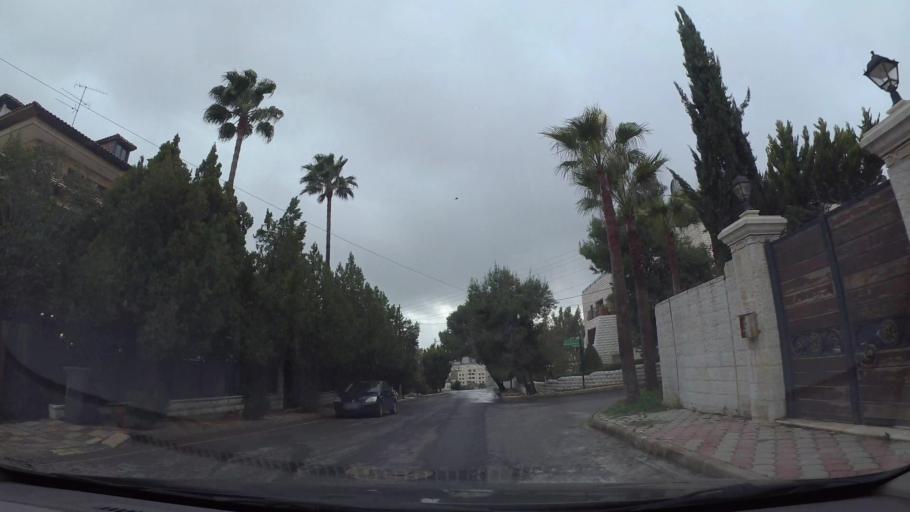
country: JO
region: Amman
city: Al Bunayyat ash Shamaliyah
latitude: 31.9480
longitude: 35.8888
